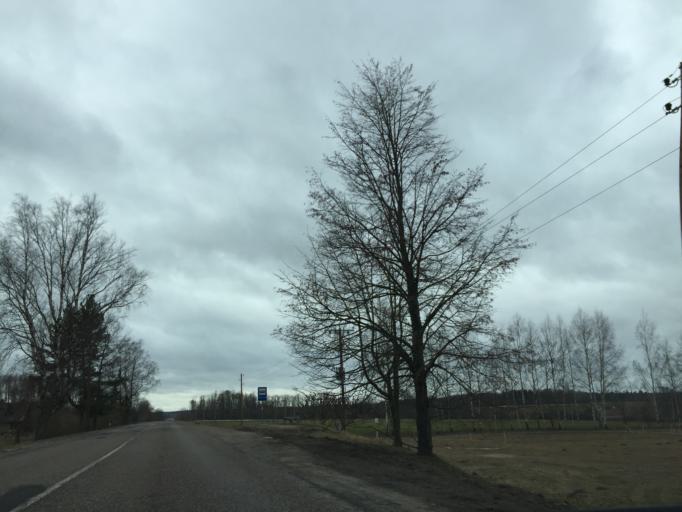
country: LV
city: Tervete
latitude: 56.5154
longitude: 23.4836
